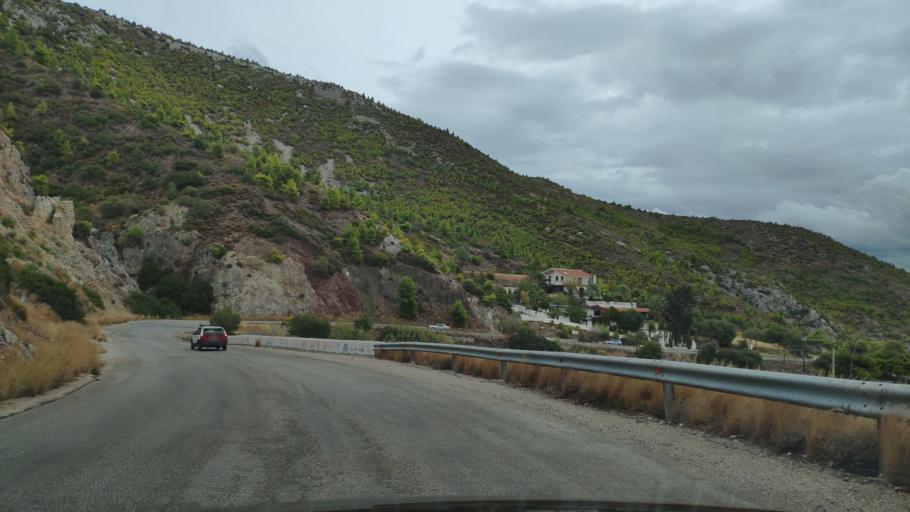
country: GR
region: Peloponnese
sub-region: Nomos Korinthias
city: Perachora
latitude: 38.0006
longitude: 22.9444
